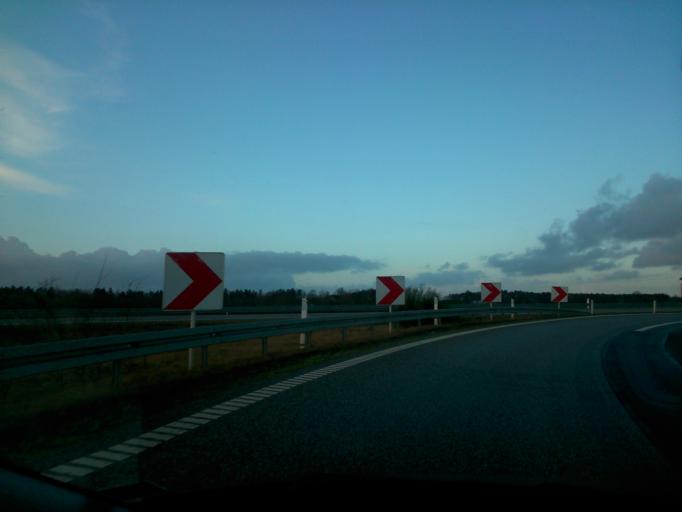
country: DK
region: Central Jutland
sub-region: Herning Kommune
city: Lind
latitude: 56.1096
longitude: 9.0104
